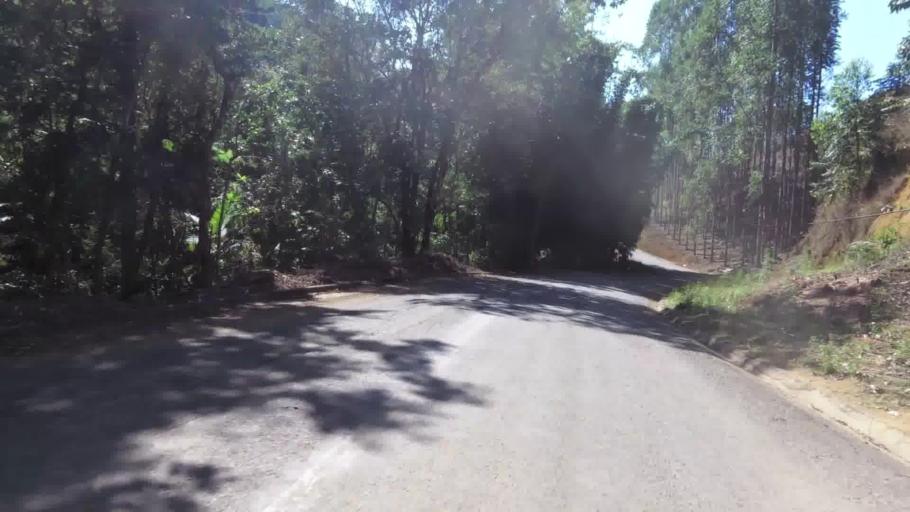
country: BR
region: Espirito Santo
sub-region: Vargem Alta
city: Vargem Alta
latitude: -20.4562
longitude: -40.9196
